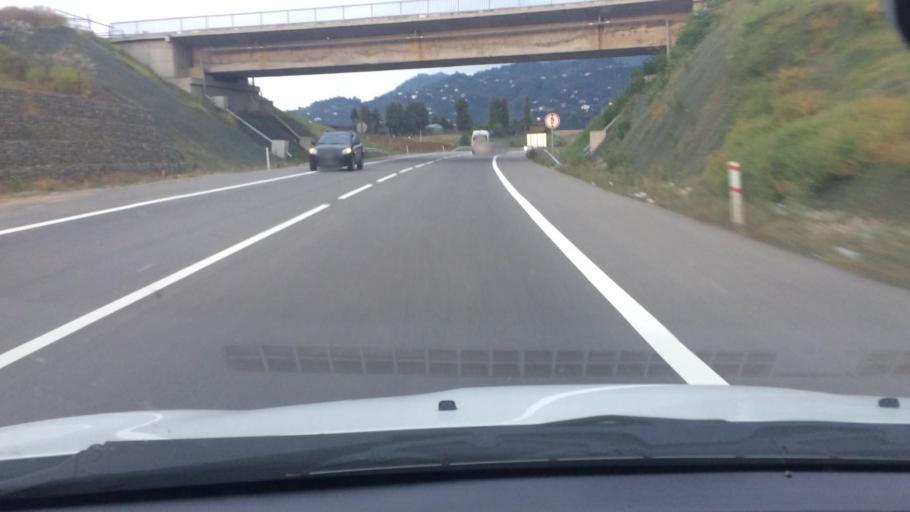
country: GE
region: Ajaria
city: Makhinjauri
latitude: 41.7067
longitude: 41.7414
